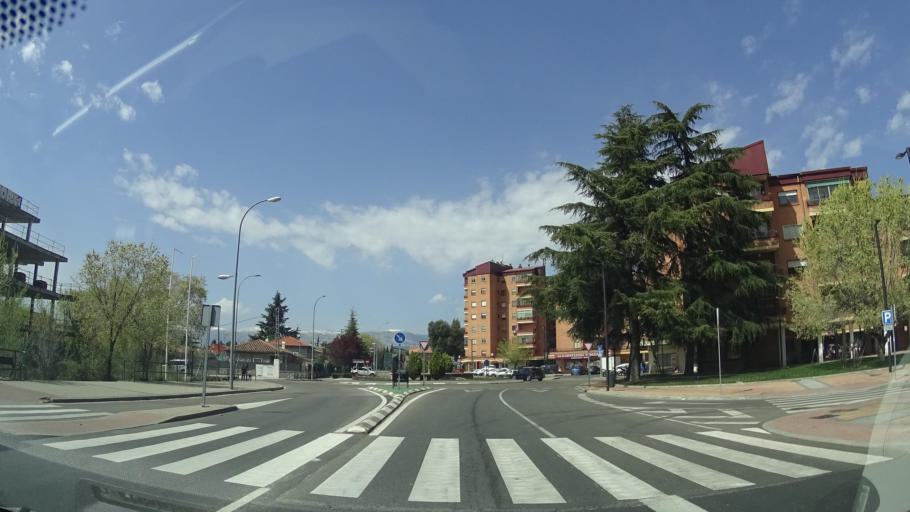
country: ES
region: Madrid
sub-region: Provincia de Madrid
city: Colmenar Viejo
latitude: 40.6692
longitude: -3.7727
